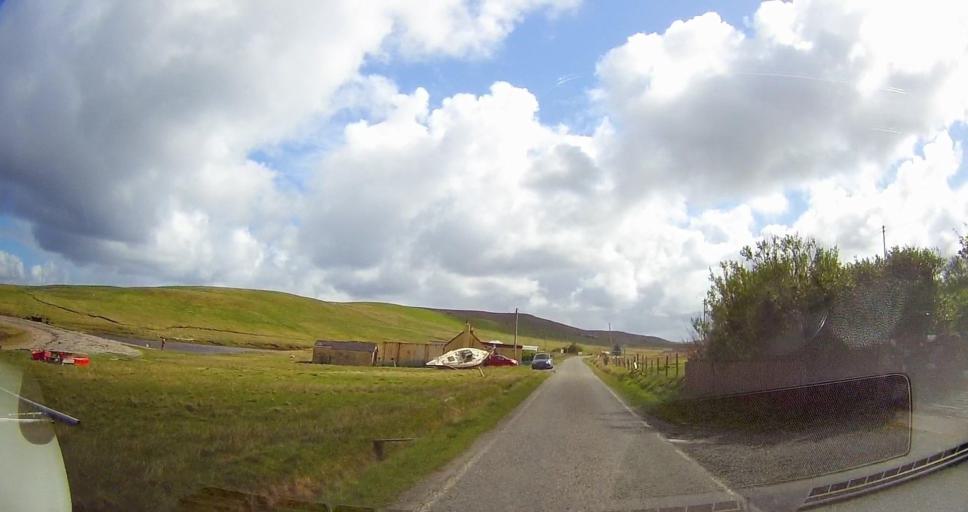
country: GB
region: Scotland
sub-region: Shetland Islands
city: Lerwick
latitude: 60.5774
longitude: -1.3316
